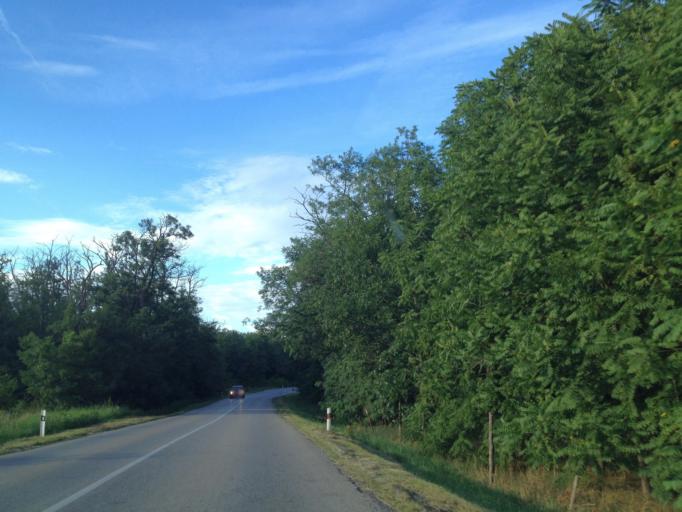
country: SK
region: Nitriansky
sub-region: Okres Komarno
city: Hurbanovo
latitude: 47.8313
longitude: 18.2376
